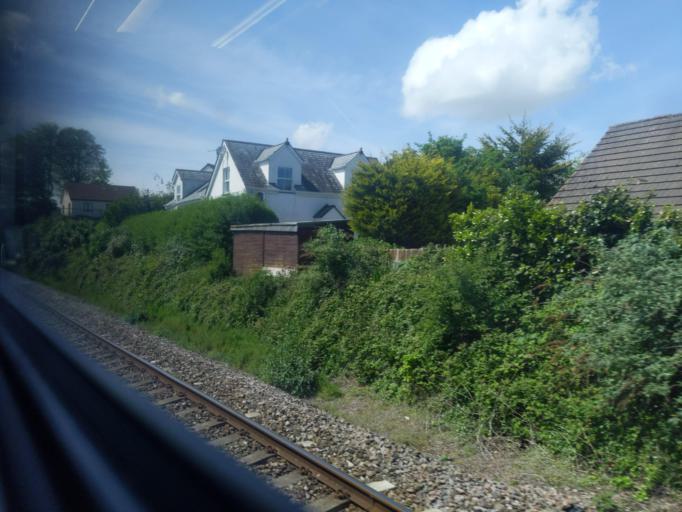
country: GB
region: England
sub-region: Cornwall
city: St Austell
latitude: 50.3402
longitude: -4.8215
